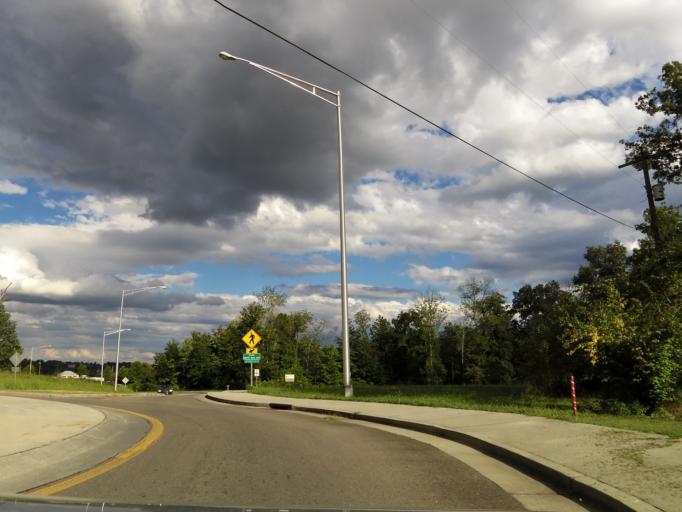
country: US
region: Tennessee
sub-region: Knox County
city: Knoxville
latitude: 36.0282
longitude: -83.8887
